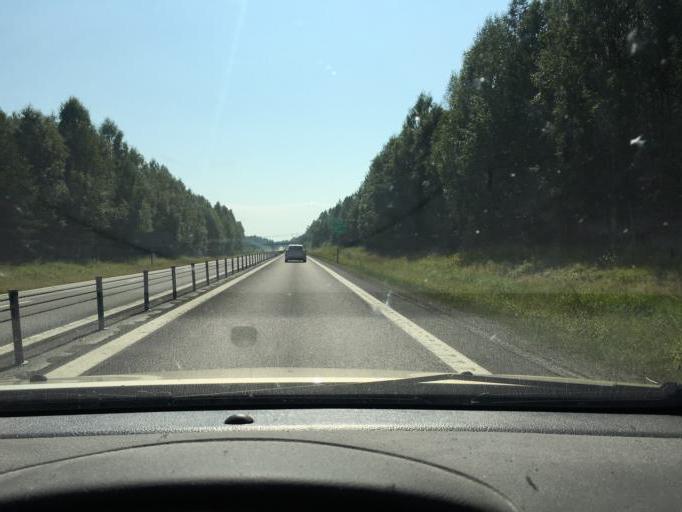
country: SE
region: Norrbotten
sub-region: Lulea Kommun
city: Gammelstad
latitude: 65.6318
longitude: 22.0629
